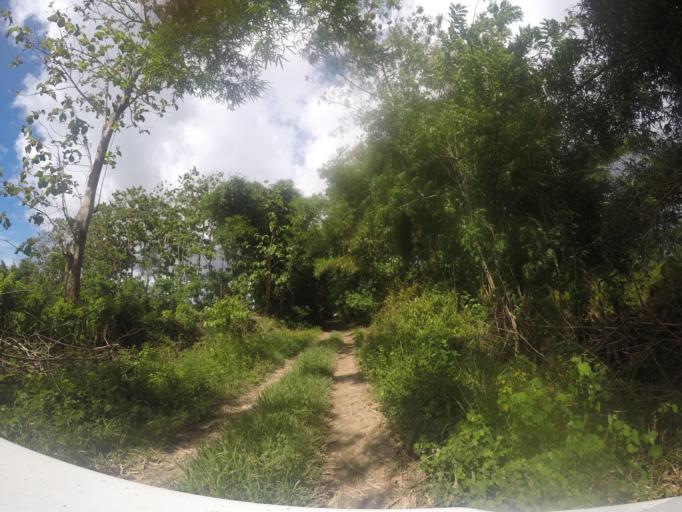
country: TL
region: Lautem
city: Lospalos
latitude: -8.4951
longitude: 127.0003
